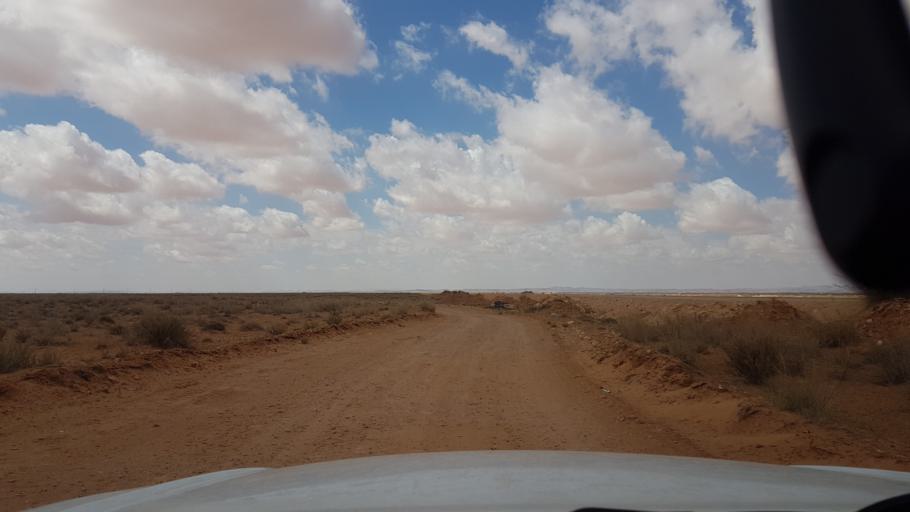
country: TN
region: Madanin
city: Medenine
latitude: 33.2730
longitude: 10.5893
